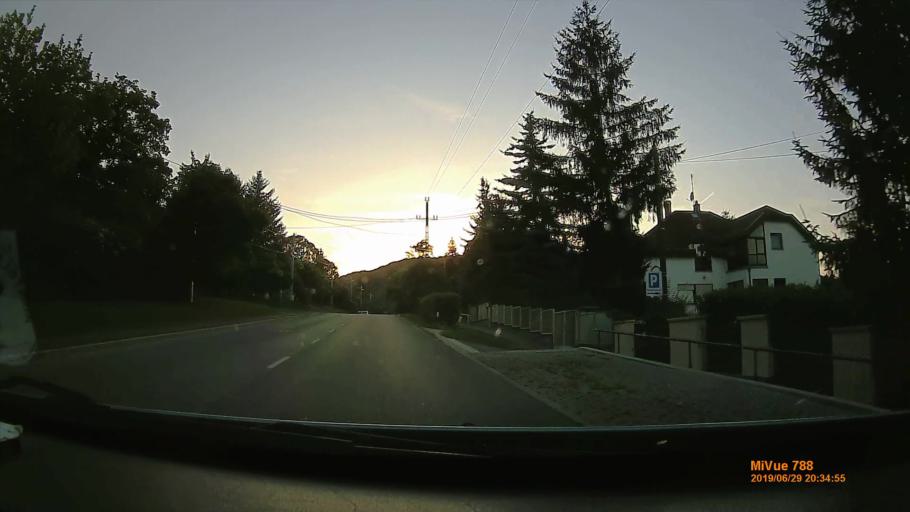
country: HU
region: Pest
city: Solymar
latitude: 47.5562
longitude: 18.9445
